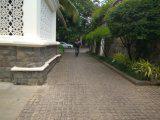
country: IN
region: Goa
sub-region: North Goa
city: Bambolim
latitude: 15.4521
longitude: 73.8518
